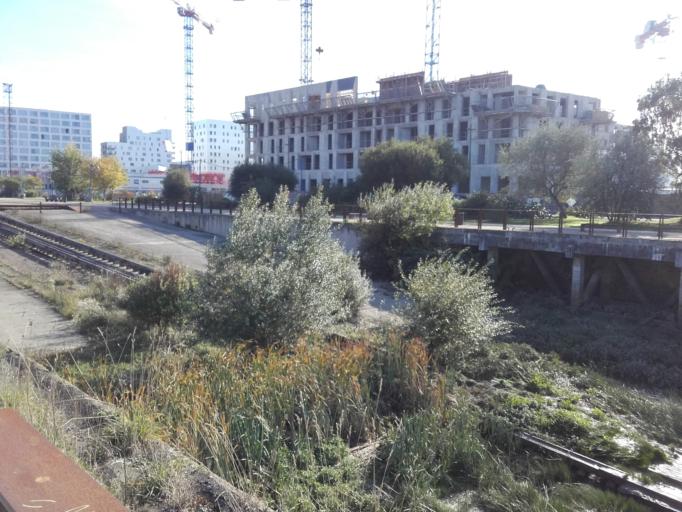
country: FR
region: Pays de la Loire
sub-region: Departement de la Loire-Atlantique
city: Nantes
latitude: 47.2048
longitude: -1.5709
